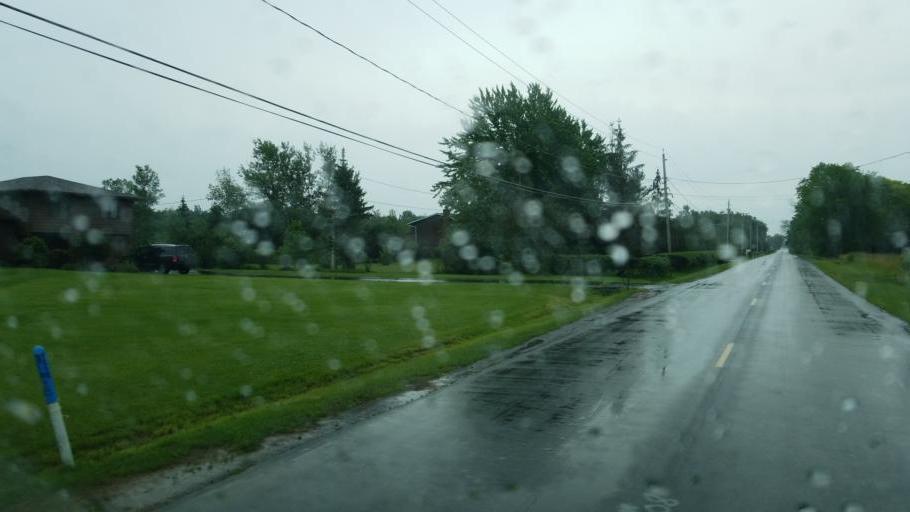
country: US
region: New York
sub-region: Niagara County
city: Ransomville
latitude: 43.2598
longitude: -78.8923
